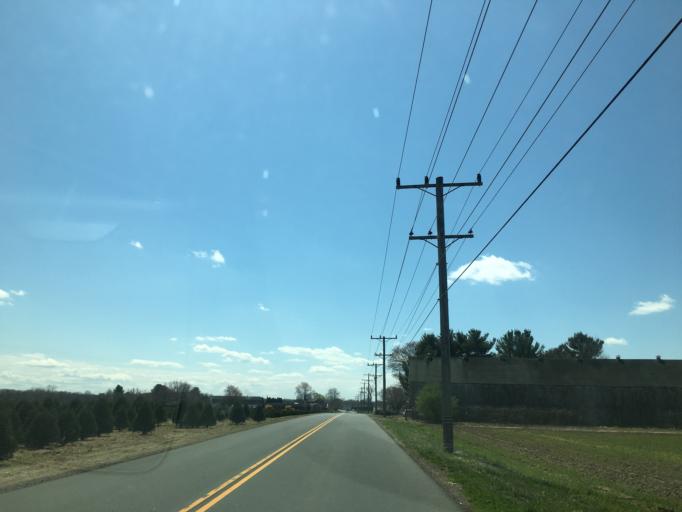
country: US
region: Connecticut
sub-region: Hartford County
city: Hazardville
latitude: 41.9993
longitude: -72.5301
